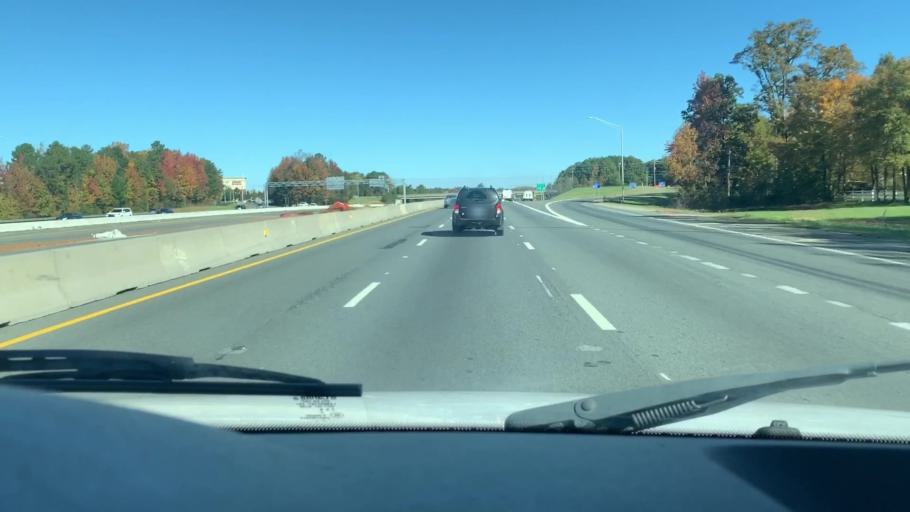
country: US
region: North Carolina
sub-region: Mecklenburg County
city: Huntersville
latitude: 35.3439
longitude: -80.8482
